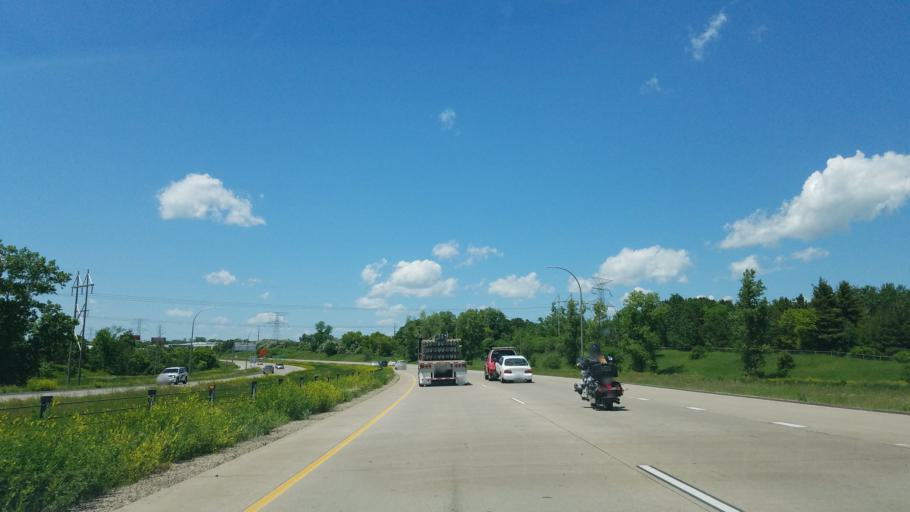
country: US
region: Minnesota
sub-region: Washington County
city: Birchwood
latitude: 45.0307
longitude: -92.9631
